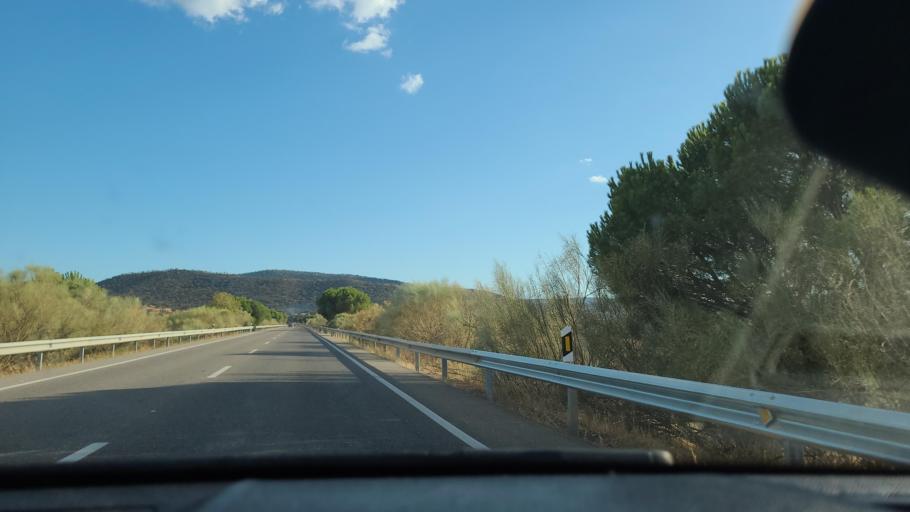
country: ES
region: Andalusia
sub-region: Province of Cordoba
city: Belmez
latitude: 38.2406
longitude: -5.1676
